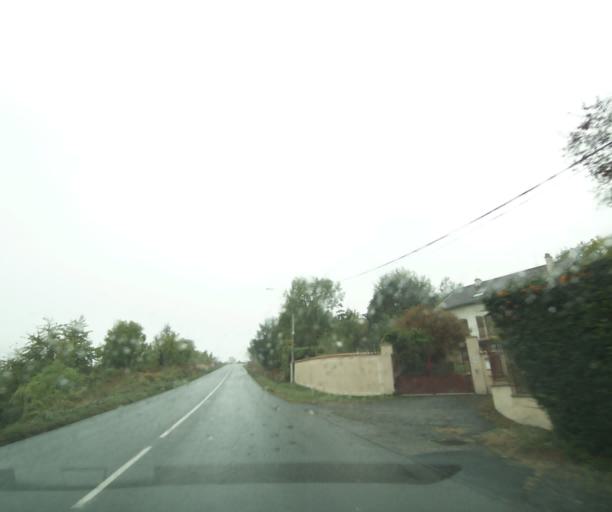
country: FR
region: Auvergne
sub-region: Departement du Puy-de-Dome
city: Chateaugay
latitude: 45.8438
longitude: 3.0876
